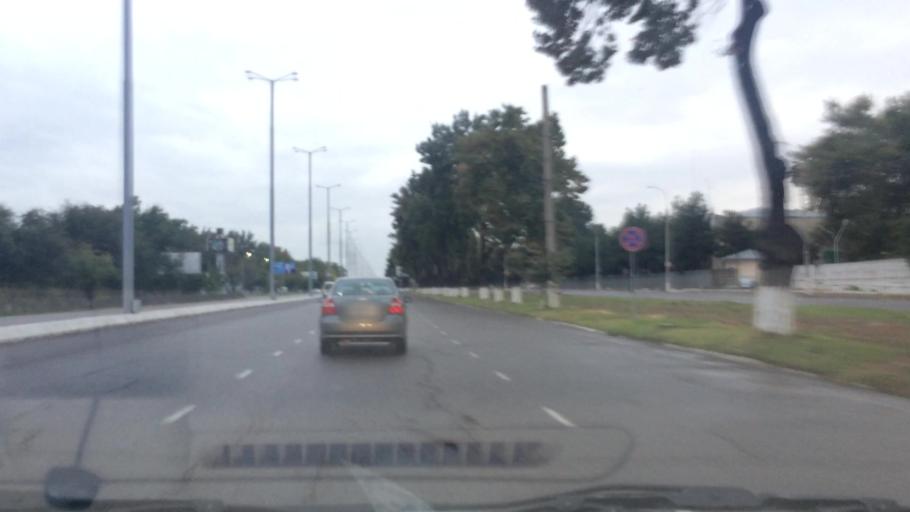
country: UZ
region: Toshkent Shahri
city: Tashkent
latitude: 41.2551
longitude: 69.1908
